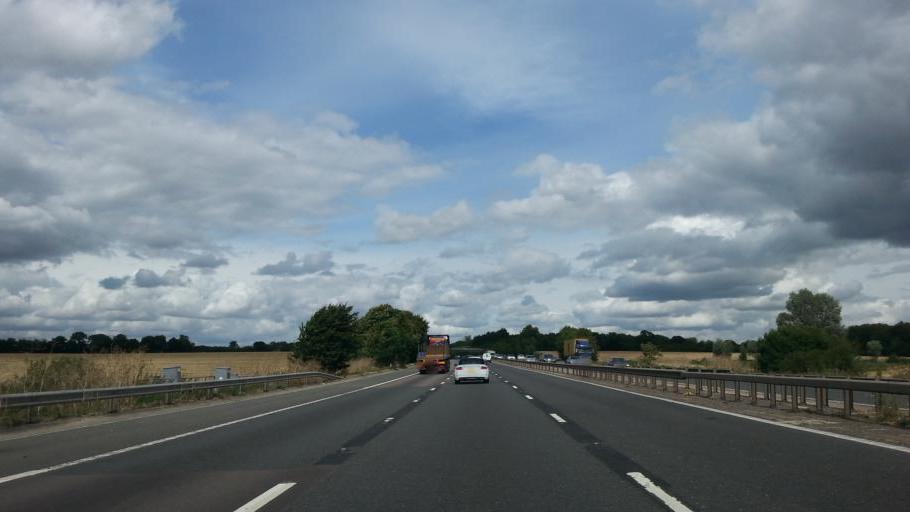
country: GB
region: England
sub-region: Hertfordshire
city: Sawbridgeworth
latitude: 51.7957
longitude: 0.1741
